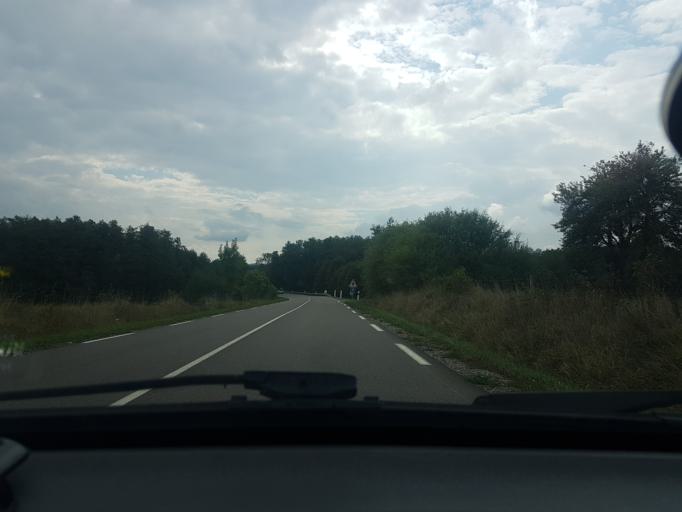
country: FR
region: Franche-Comte
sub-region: Departement du Doubs
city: Arcey
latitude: 47.5727
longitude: 6.6548
